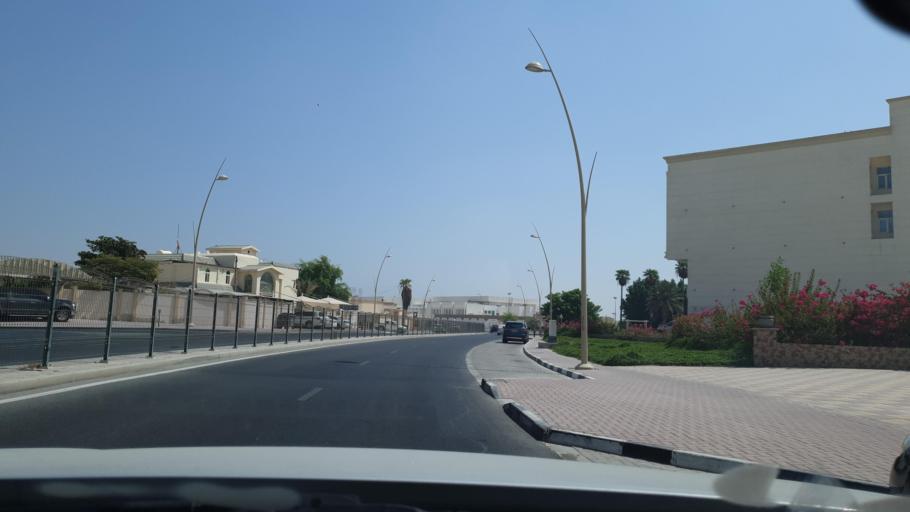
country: QA
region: Al Khawr
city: Al Khawr
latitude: 25.6837
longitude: 51.5114
